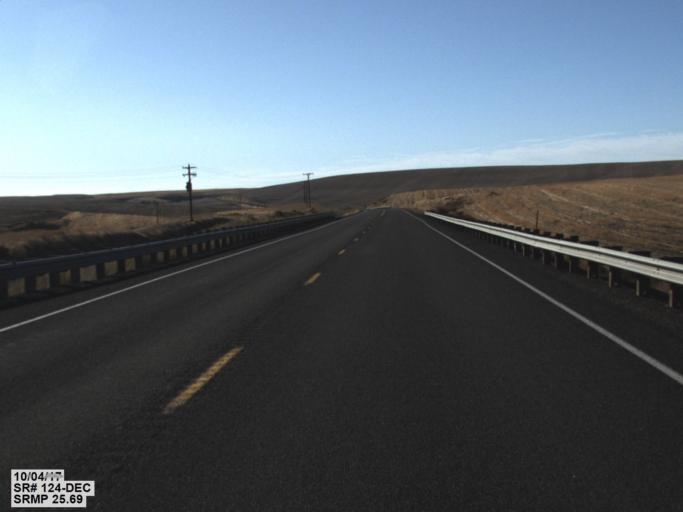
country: US
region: Washington
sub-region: Walla Walla County
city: Garrett
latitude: 46.2908
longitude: -118.5244
